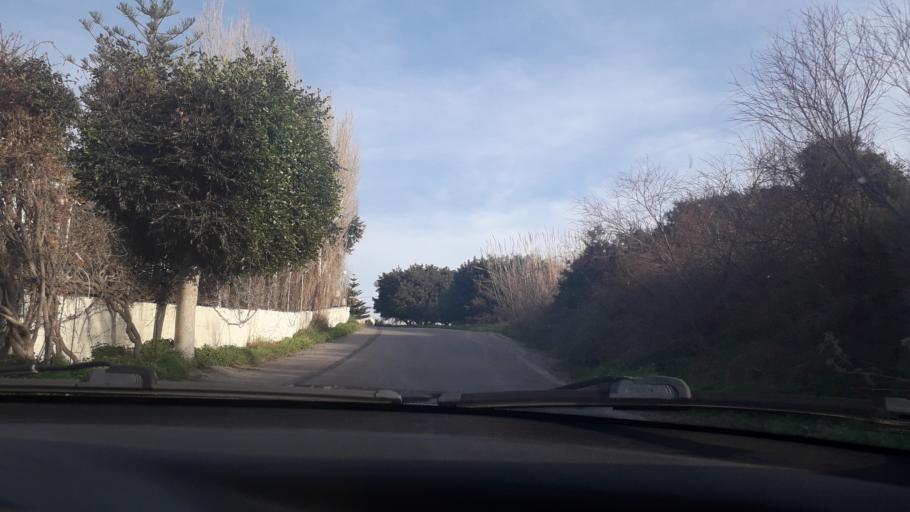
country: GR
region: Crete
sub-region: Nomos Rethymnis
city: Panormos
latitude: 35.3898
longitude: 24.6126
